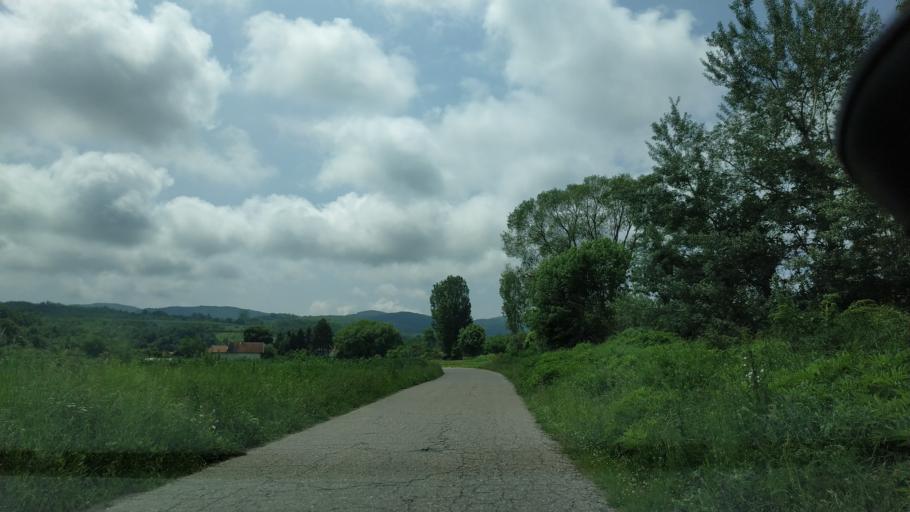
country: RS
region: Central Serbia
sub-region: Nisavski Okrug
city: Aleksinac
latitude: 43.4307
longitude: 21.7110
